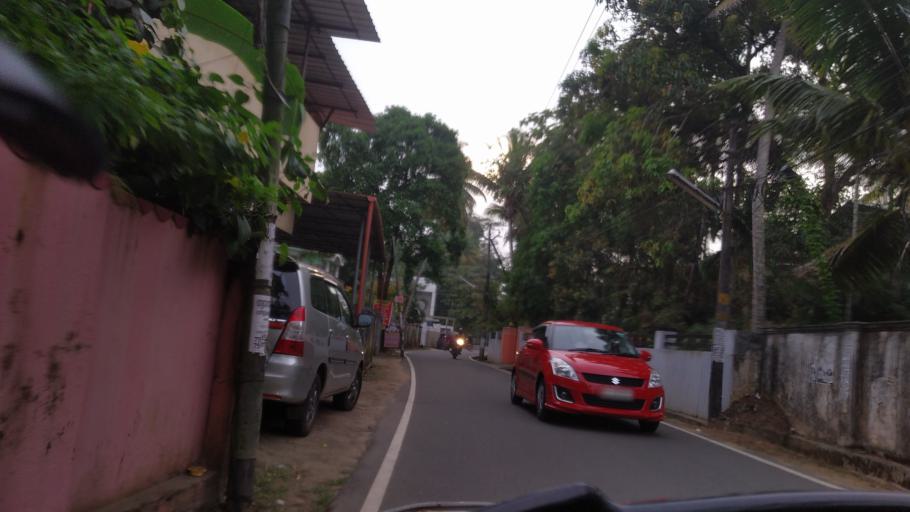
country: IN
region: Kerala
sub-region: Thrissur District
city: Kodungallur
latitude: 10.1383
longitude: 76.2268
